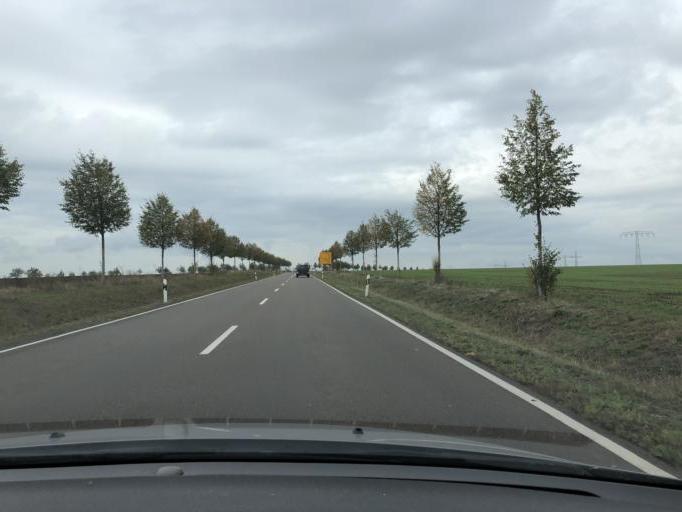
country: DE
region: Saxony-Anhalt
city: Reichardtswerben
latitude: 51.2228
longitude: 11.9462
